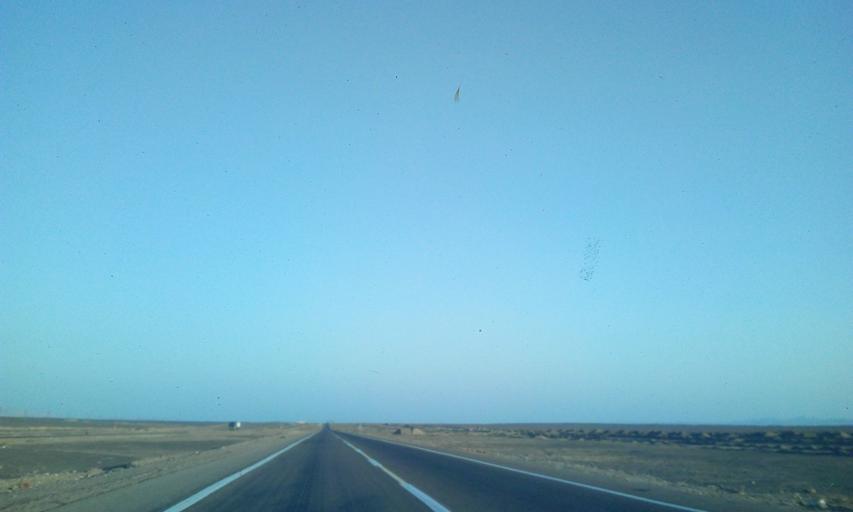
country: EG
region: South Sinai
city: Tor
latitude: 28.0394
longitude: 33.2891
